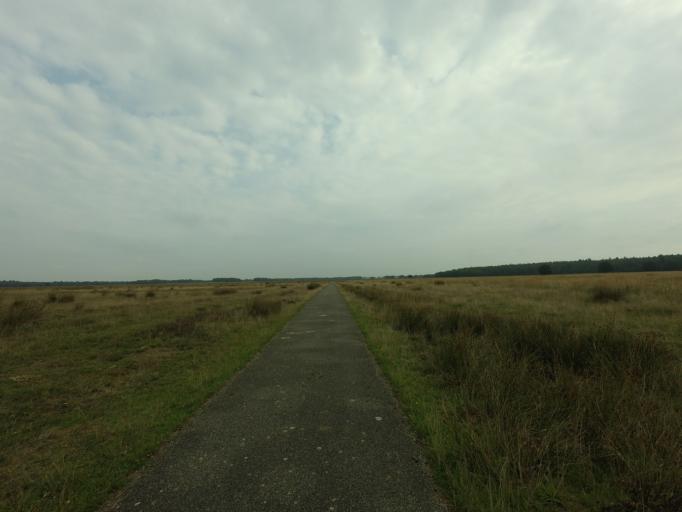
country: NL
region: Drenthe
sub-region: Gemeente Assen
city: Assen
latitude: 52.9140
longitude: 6.4912
